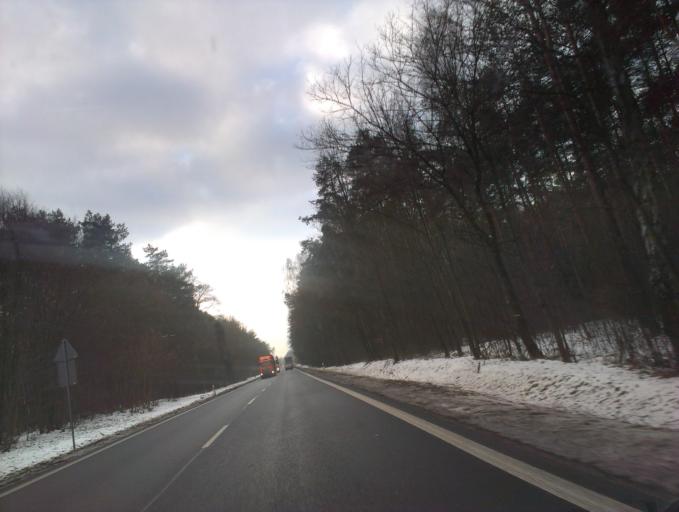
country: PL
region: Greater Poland Voivodeship
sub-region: Powiat zlotowski
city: Jastrowie
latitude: 53.4371
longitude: 16.8358
